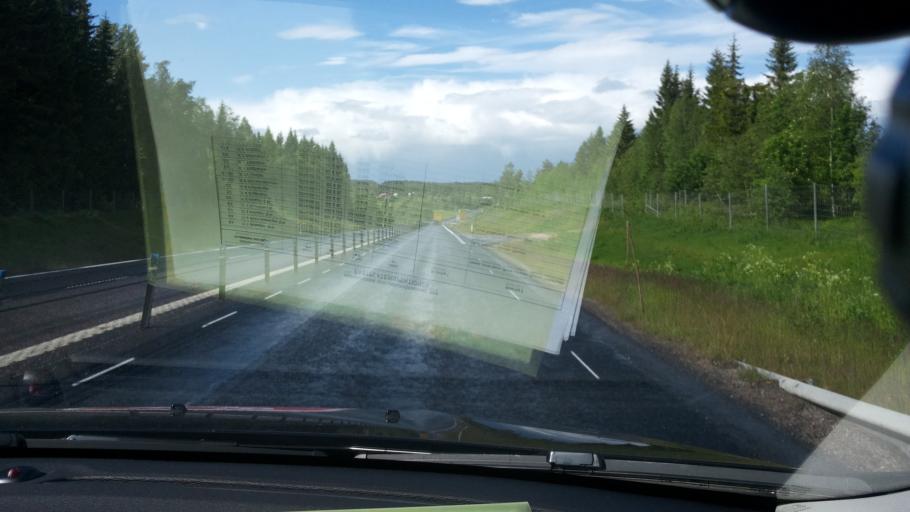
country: SE
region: Vaesternorrland
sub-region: Sundsvalls Kommun
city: Njurundabommen
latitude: 62.2176
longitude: 17.3727
